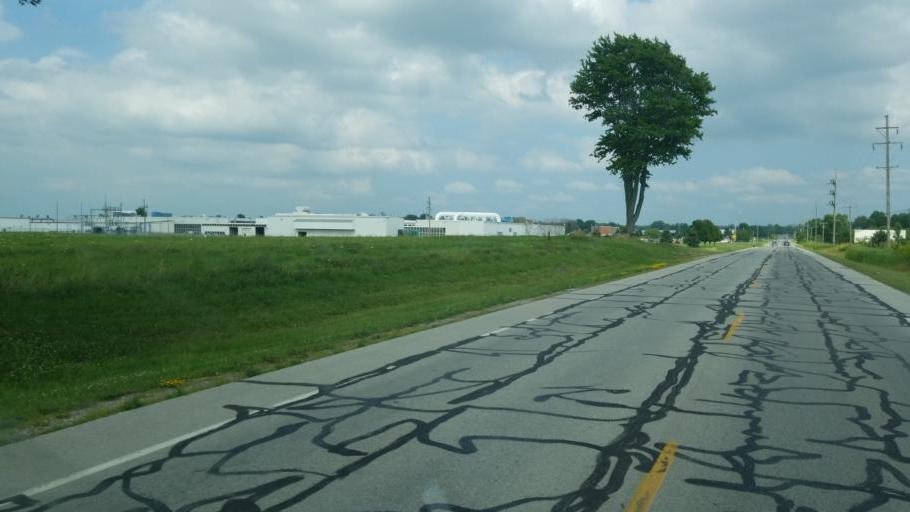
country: US
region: Ohio
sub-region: Crawford County
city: Crestline
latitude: 40.7865
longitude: -82.7049
